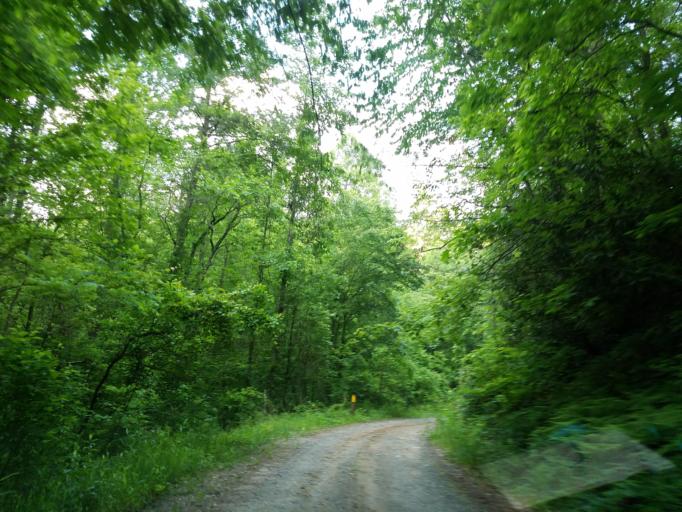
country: US
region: Georgia
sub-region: Dawson County
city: Dawsonville
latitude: 34.5693
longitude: -84.1374
